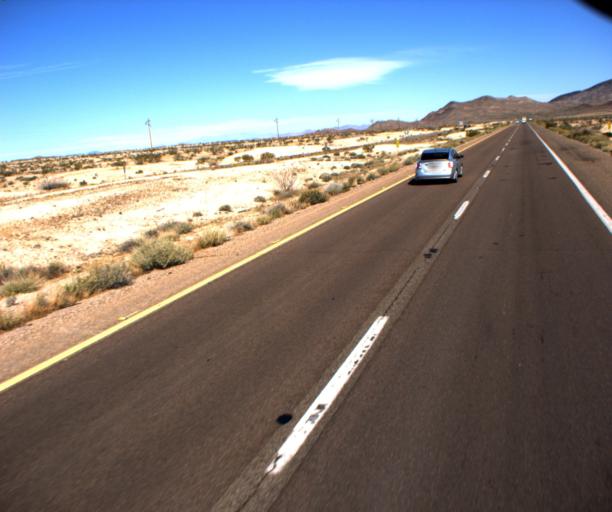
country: US
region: Nevada
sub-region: Clark County
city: Boulder City
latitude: 35.8254
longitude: -114.5571
